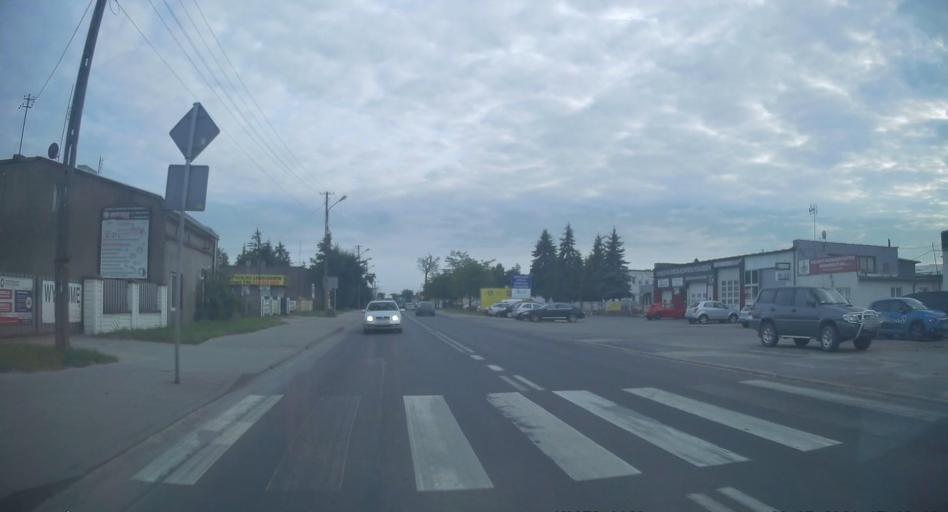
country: PL
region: Lodz Voivodeship
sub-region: Powiat radomszczanski
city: Radomsko
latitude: 51.0825
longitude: 19.4521
